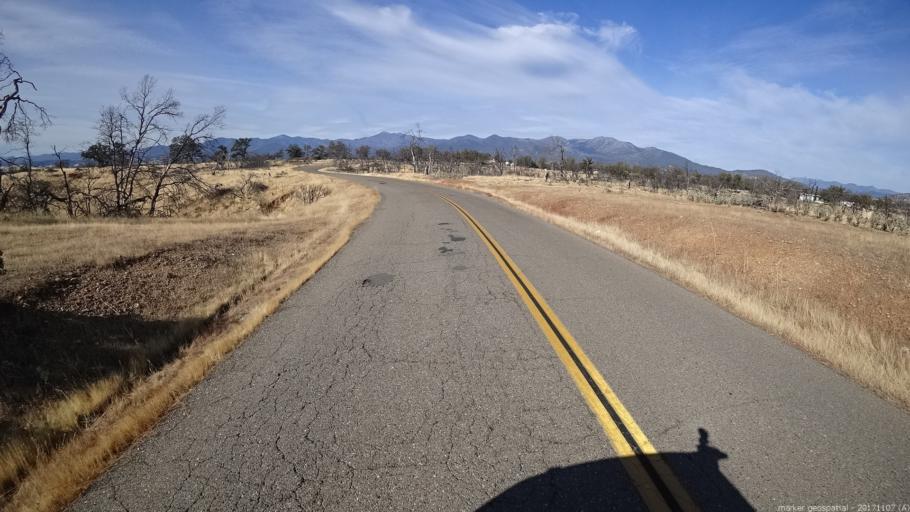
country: US
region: California
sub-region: Shasta County
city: Shasta
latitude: 40.4622
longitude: -122.5370
